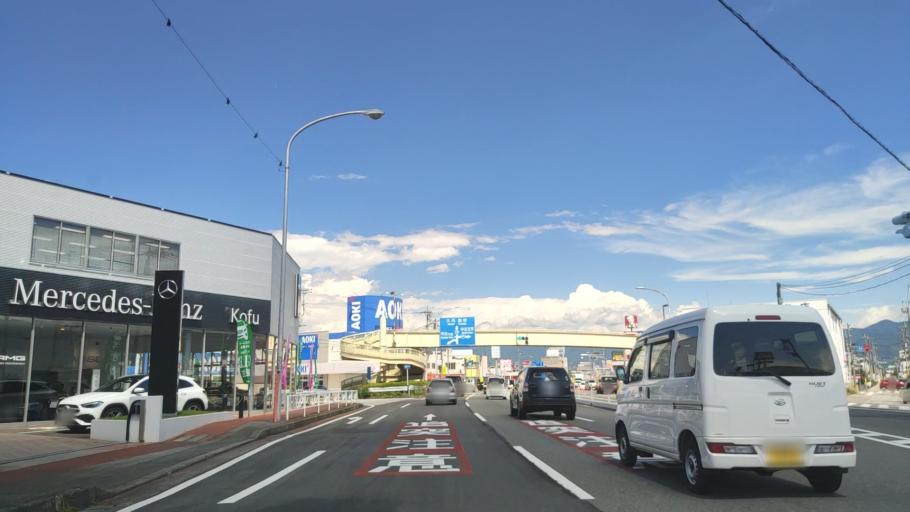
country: JP
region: Yamanashi
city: Isawa
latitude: 35.6458
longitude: 138.6063
